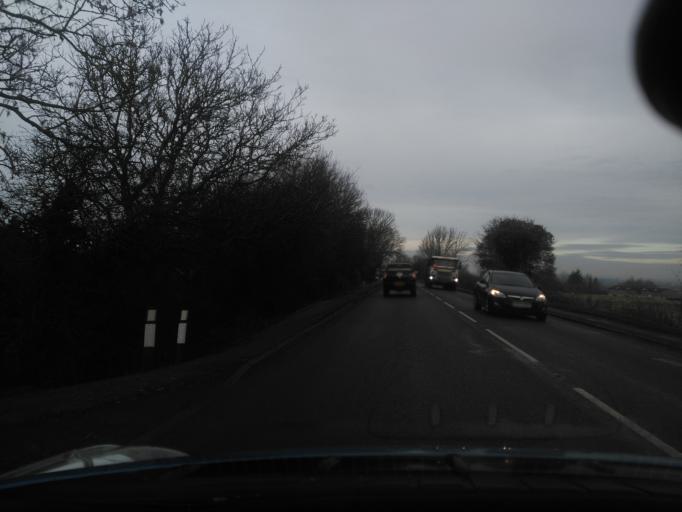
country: GB
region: England
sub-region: Worcestershire
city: Badsey
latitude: 52.0611
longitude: -1.8911
